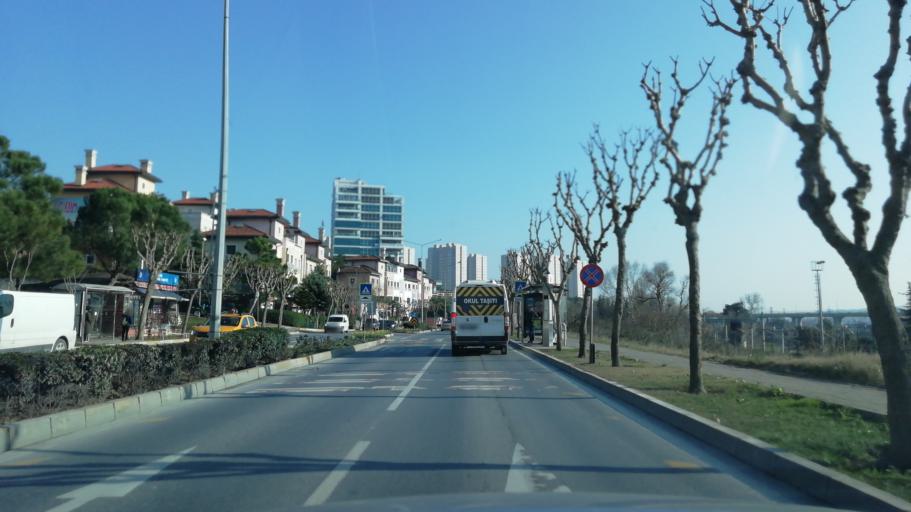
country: TR
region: Istanbul
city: Esenyurt
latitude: 41.0662
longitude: 28.6976
